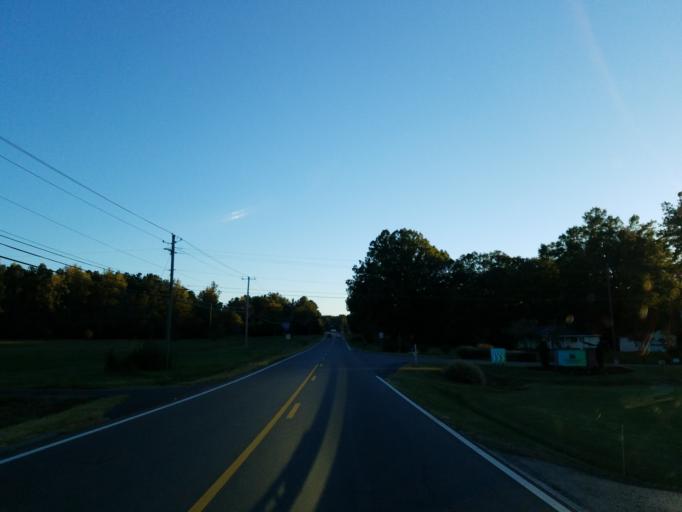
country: US
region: Georgia
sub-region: Forsyth County
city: Cumming
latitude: 34.2674
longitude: -84.1025
